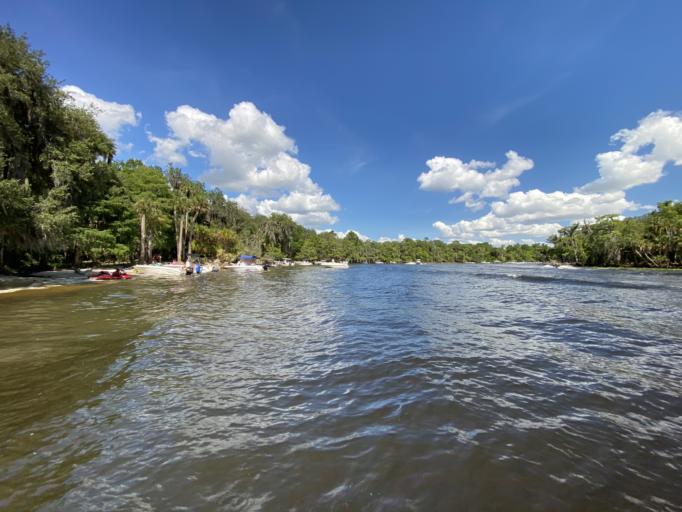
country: US
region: Florida
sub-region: Volusia County
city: DeBary
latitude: 28.8636
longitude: -81.3539
